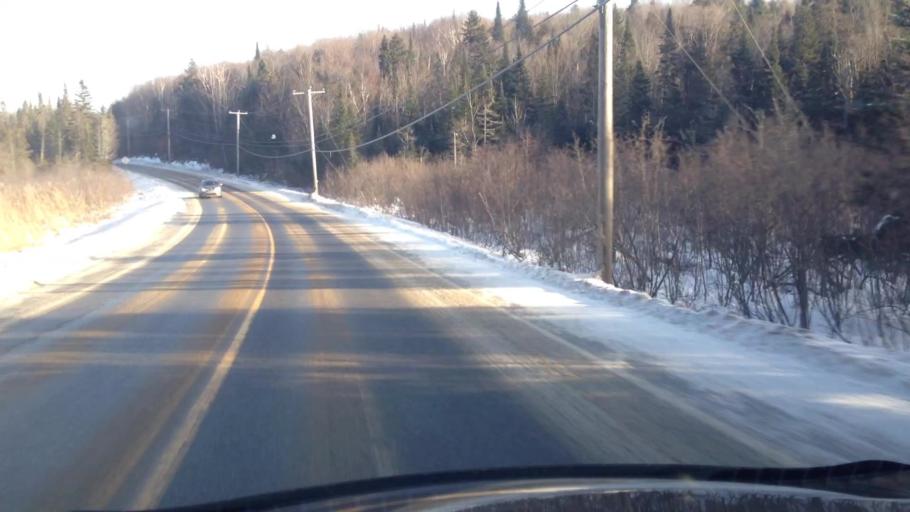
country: CA
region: Quebec
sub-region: Laurentides
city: Sainte-Agathe-des-Monts
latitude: 45.9102
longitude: -74.3531
